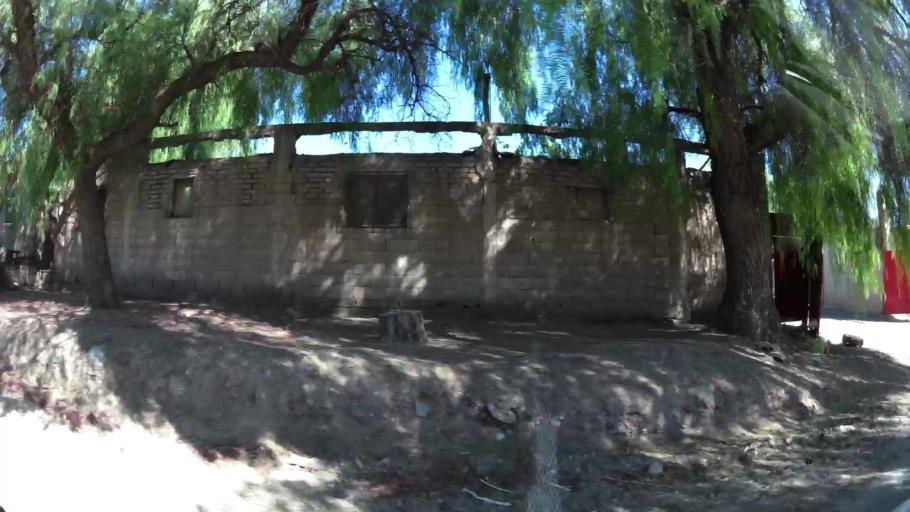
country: AR
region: Mendoza
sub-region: Departamento de Godoy Cruz
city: Godoy Cruz
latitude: -32.9102
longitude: -68.8802
